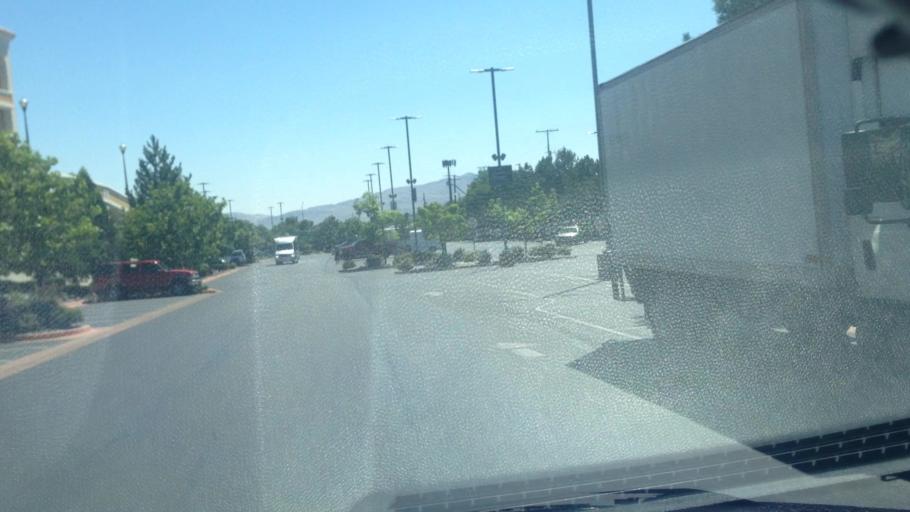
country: US
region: Nevada
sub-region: Washoe County
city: Reno
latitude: 39.4960
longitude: -119.8012
